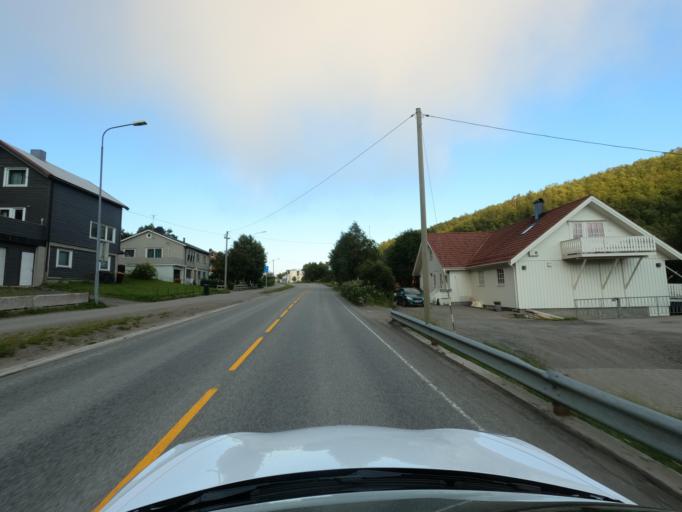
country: NO
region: Troms
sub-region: Harstad
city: Harstad
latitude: 68.8056
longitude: 16.5186
